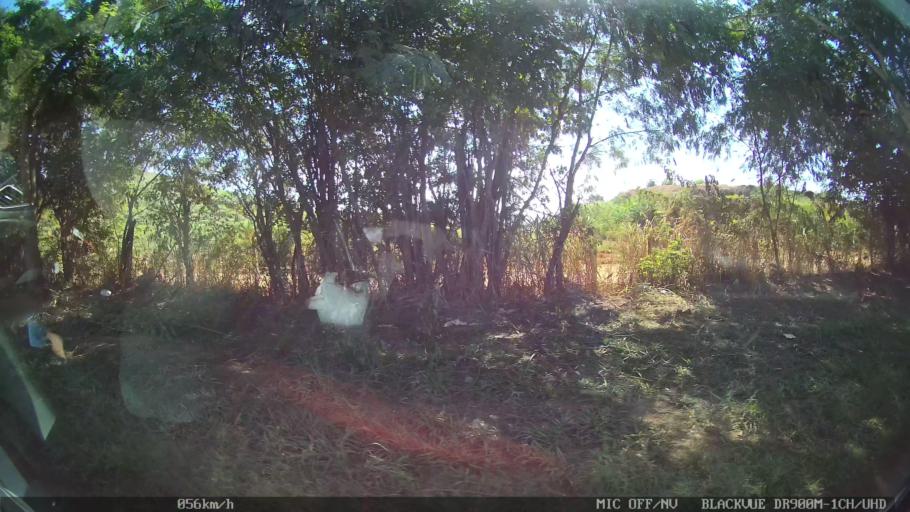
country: BR
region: Sao Paulo
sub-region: Santa Barbara D'Oeste
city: Santa Barbara d'Oeste
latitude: -22.7249
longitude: -47.4217
